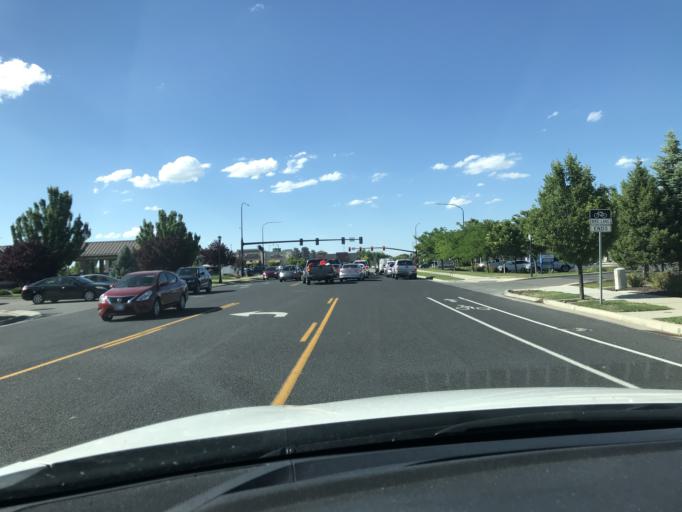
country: US
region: Utah
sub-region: Salt Lake County
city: South Jordan Heights
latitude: 40.5605
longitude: -111.9721
